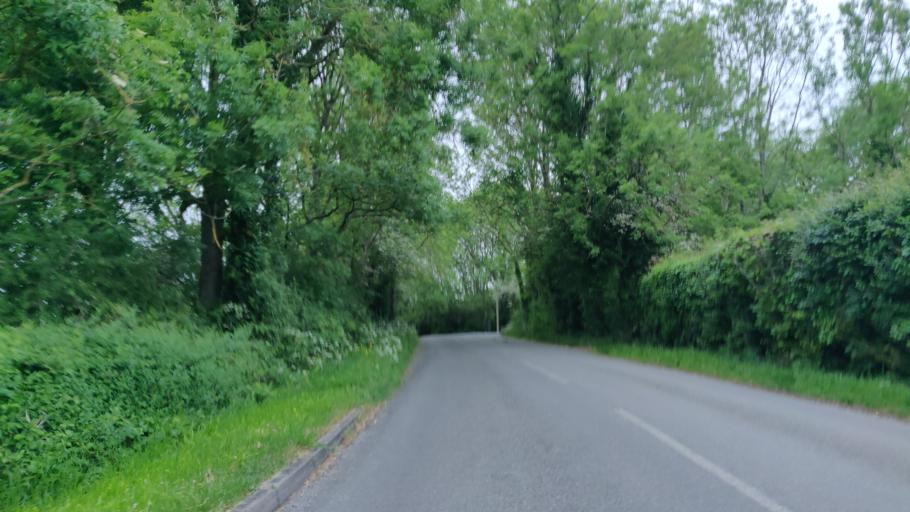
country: GB
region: England
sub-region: West Sussex
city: Southwater
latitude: 51.0320
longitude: -0.3655
